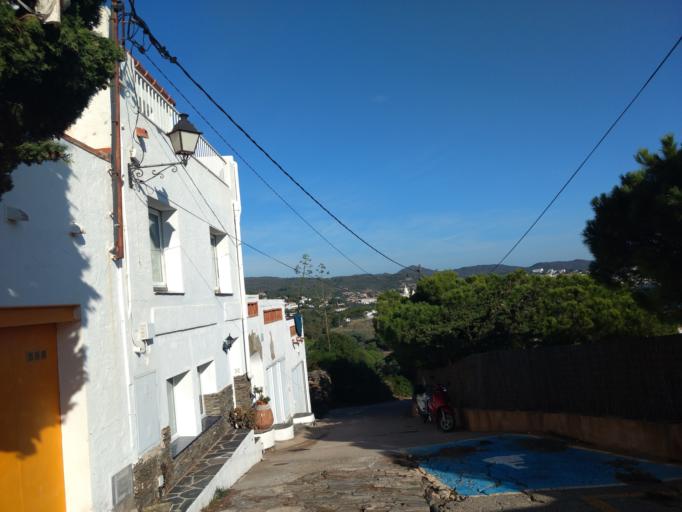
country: ES
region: Catalonia
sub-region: Provincia de Girona
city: Cadaques
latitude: 42.2786
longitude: 3.2770
